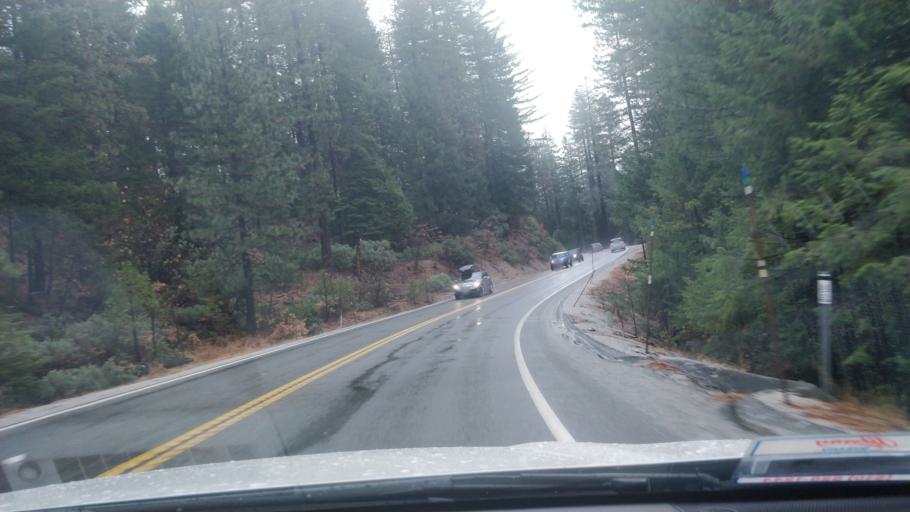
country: US
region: California
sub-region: Nevada County
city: Nevada City
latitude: 39.3220
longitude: -120.8386
